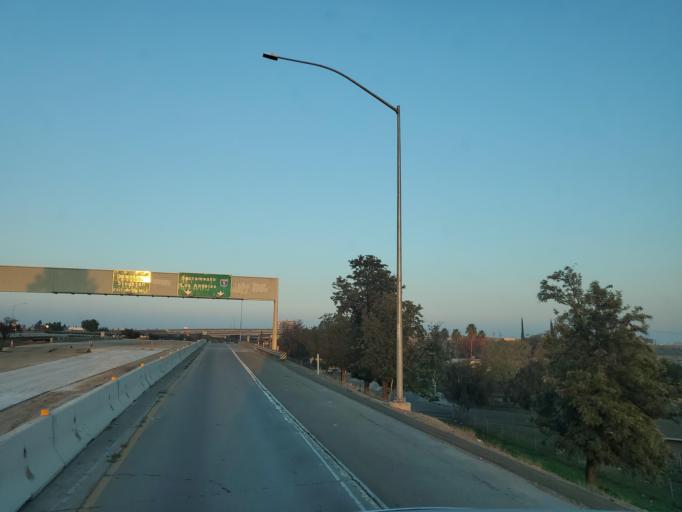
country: US
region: California
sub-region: San Joaquin County
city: Stockton
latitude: 37.9456
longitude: -121.3077
